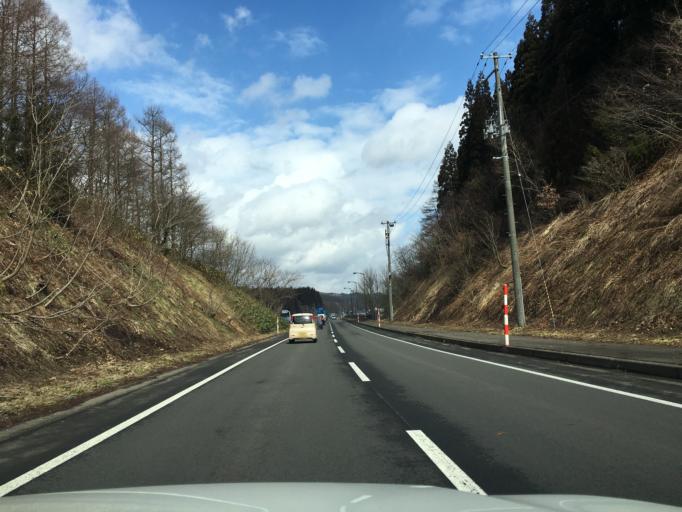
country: JP
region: Akita
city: Takanosu
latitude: 40.0284
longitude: 140.2739
